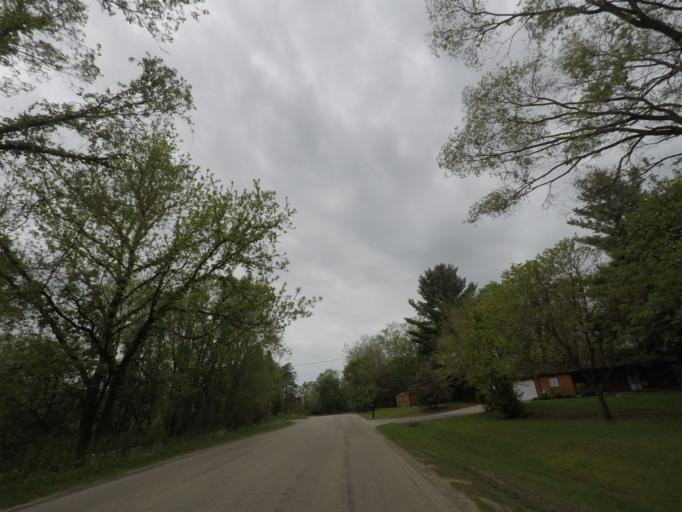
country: US
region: Illinois
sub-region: Winnebago County
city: Roscoe
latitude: 42.4086
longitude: -88.9796
